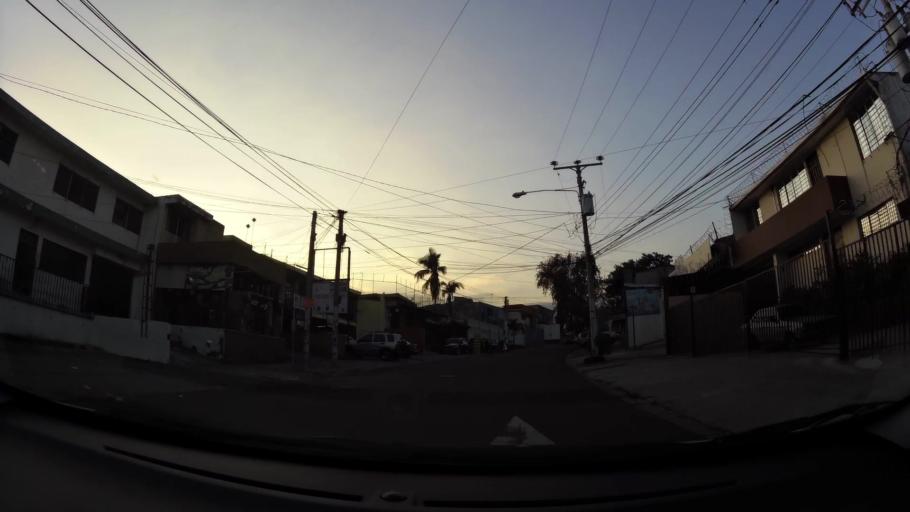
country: SV
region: San Salvador
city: San Salvador
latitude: 13.7091
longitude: -89.2080
